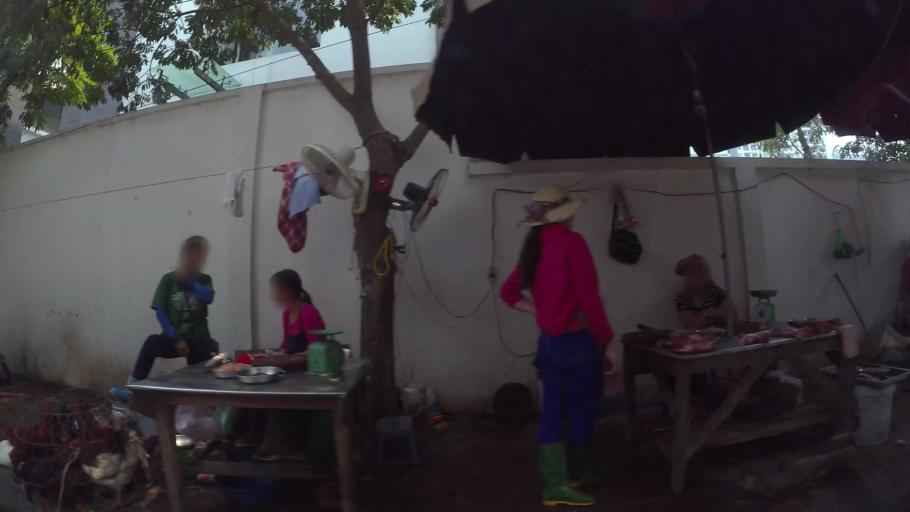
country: VN
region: Ha Noi
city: Thanh Xuan
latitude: 20.9972
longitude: 105.8009
